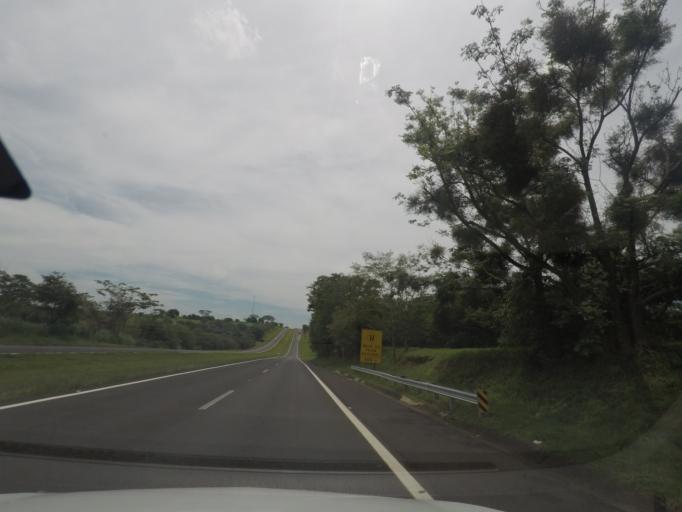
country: BR
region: Sao Paulo
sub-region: Bebedouro
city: Bebedouro
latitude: -20.9739
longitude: -48.4391
